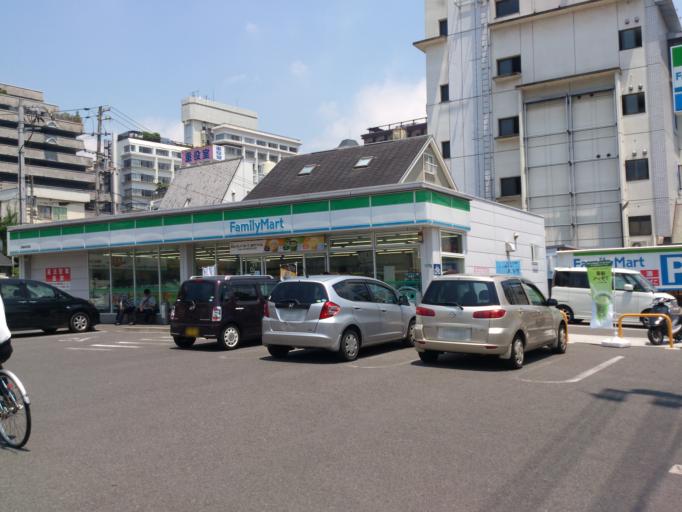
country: JP
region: Ehime
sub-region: Shikoku-chuo Shi
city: Matsuyama
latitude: 33.8522
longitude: 132.7836
